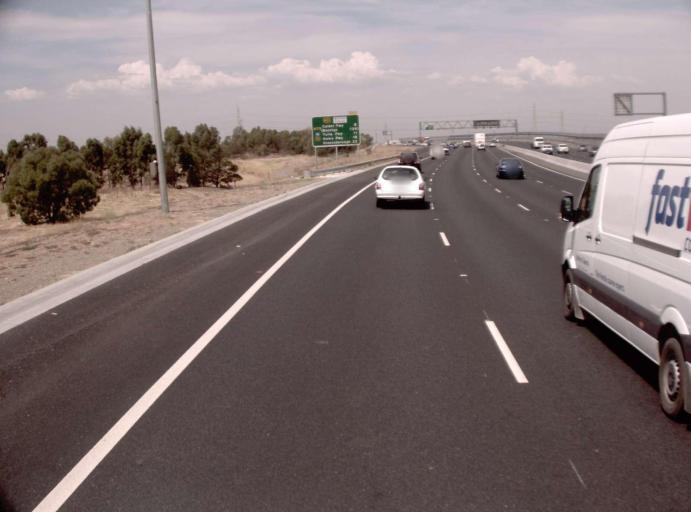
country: AU
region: Victoria
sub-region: Brimbank
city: Cairnlea
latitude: -37.7672
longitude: 144.8039
